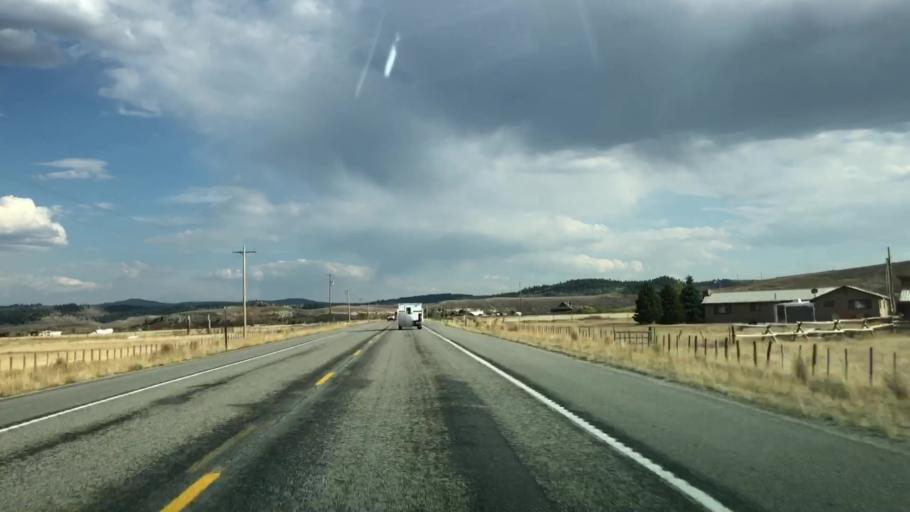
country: US
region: Wyoming
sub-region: Teton County
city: Hoback
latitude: 43.1667
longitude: -110.3746
